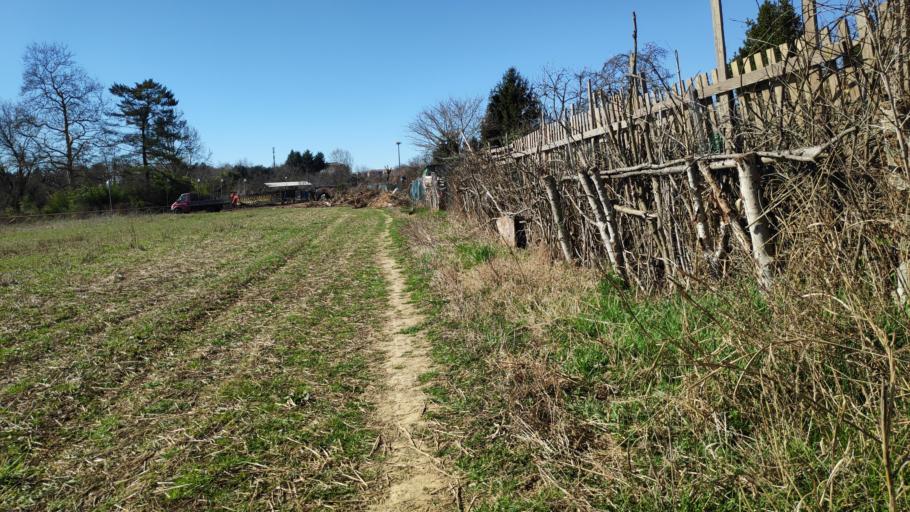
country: IT
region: Lombardy
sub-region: Citta metropolitana di Milano
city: San Giuliano Milanese
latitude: 45.4086
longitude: 9.2803
